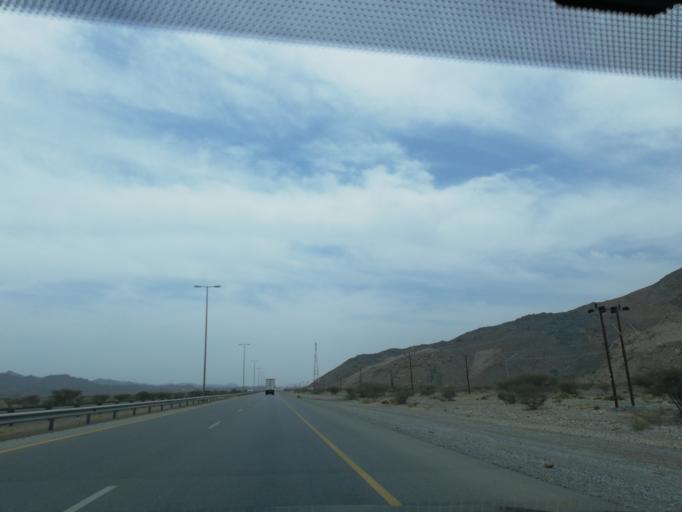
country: OM
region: Muhafazat ad Dakhiliyah
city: Izki
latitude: 23.0664
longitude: 57.8140
